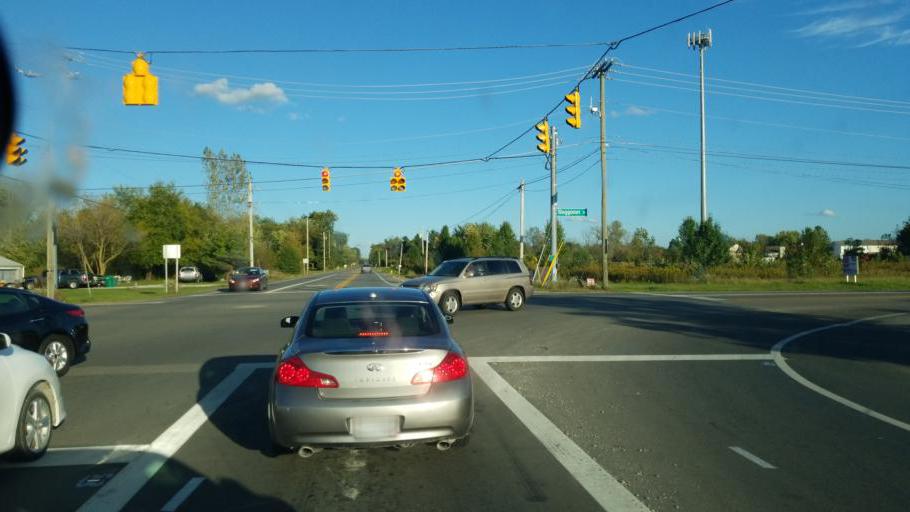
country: US
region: Ohio
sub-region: Franklin County
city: New Albany
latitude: 40.0192
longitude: -82.7900
